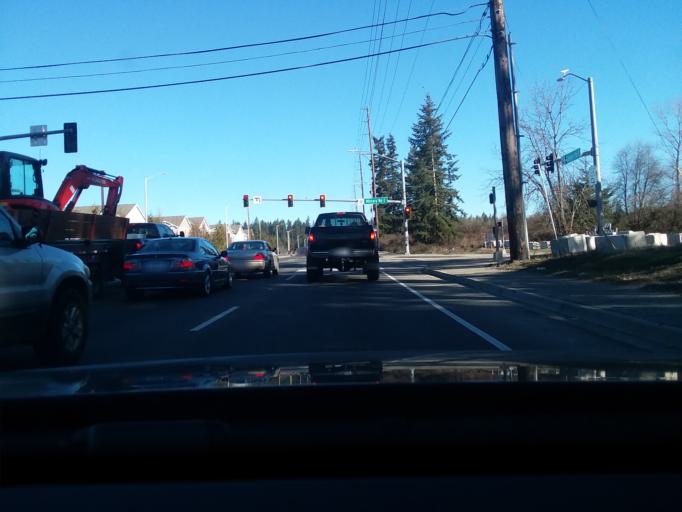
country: US
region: Washington
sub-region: Pierce County
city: Frederickson
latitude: 47.1052
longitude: -122.3575
